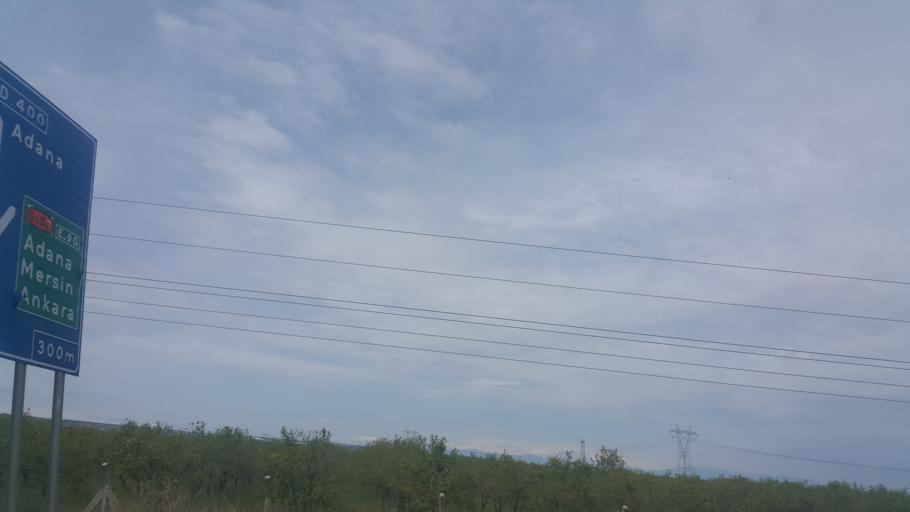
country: TR
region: Adana
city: Yakapinar
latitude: 37.0101
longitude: 35.7036
